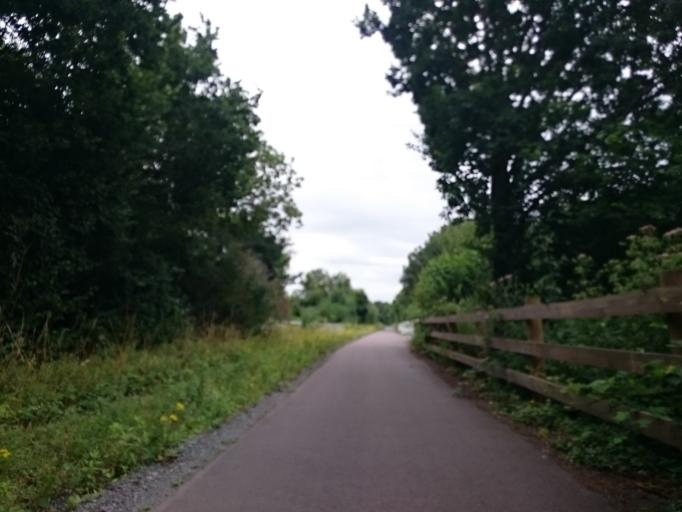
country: FR
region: Lower Normandy
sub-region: Departement du Calvados
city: Saint-Andre-sur-Orne
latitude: 49.1257
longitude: -0.4015
